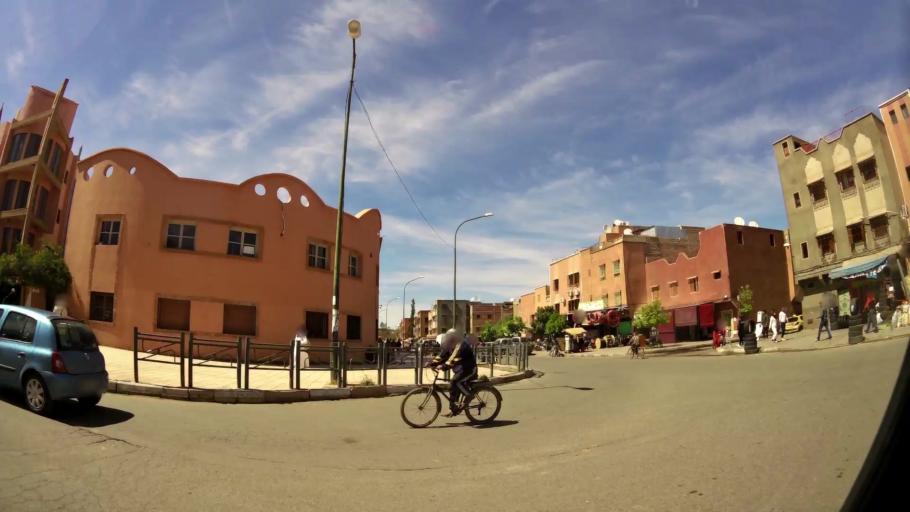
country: MA
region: Marrakech-Tensift-Al Haouz
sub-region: Marrakech
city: Marrakesh
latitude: 31.6053
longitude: -7.9630
